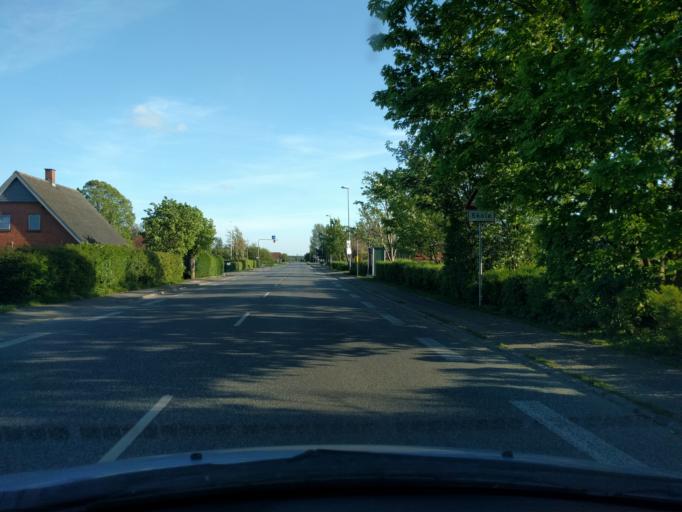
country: DK
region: Zealand
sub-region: Guldborgsund Kommune
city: Stubbekobing
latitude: 54.8015
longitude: 11.9932
